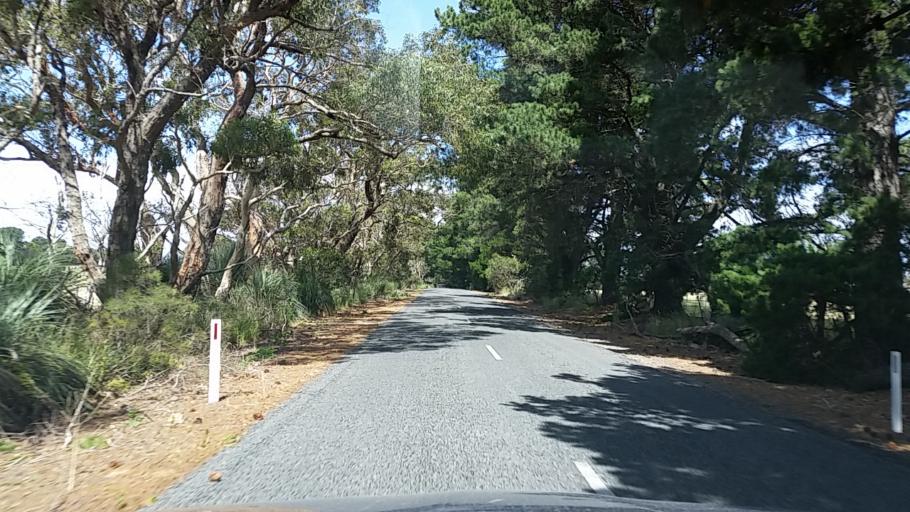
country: AU
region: South Australia
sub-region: Alexandrina
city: Mount Compass
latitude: -35.4395
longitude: 138.6130
